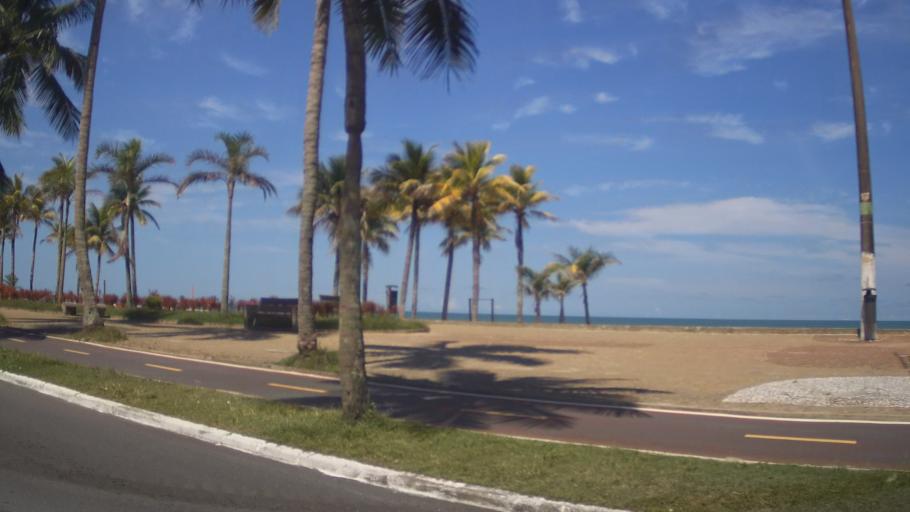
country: BR
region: Sao Paulo
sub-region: Praia Grande
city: Praia Grande
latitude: -24.0250
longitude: -46.4618
